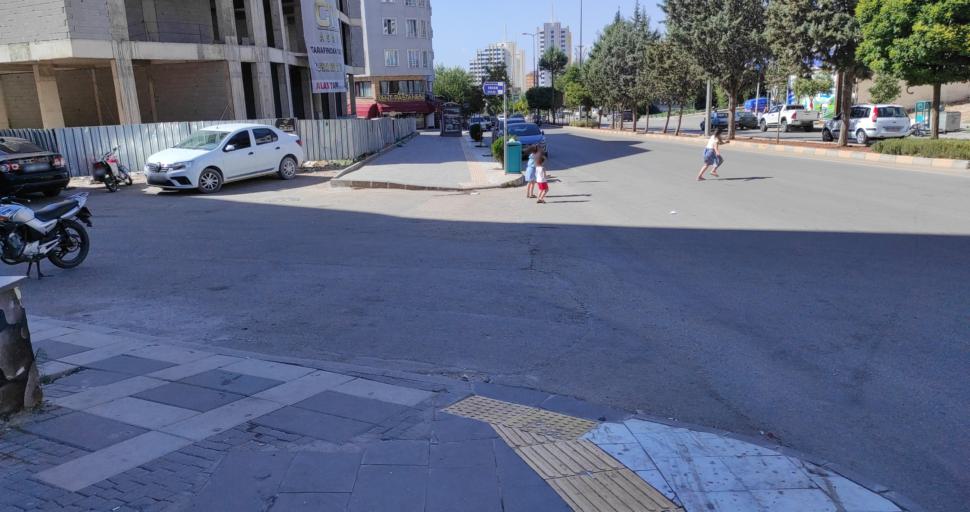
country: TR
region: Kilis
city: Kilis
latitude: 36.7277
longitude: 37.1005
